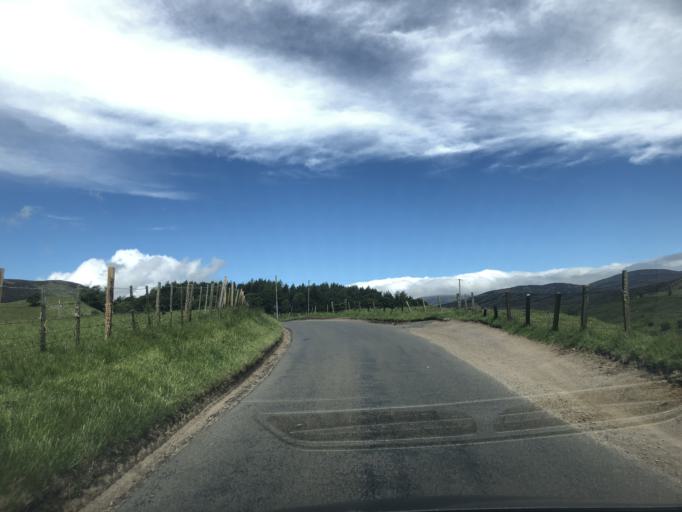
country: GB
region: Scotland
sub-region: Angus
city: Kirriemuir
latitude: 56.7600
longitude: -3.0188
